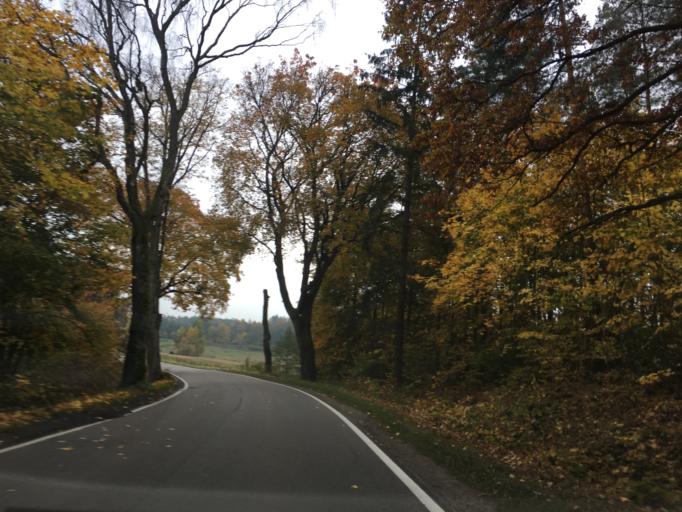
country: PL
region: Pomeranian Voivodeship
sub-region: Powiat wejherowski
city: Luzino
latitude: 54.4694
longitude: 18.0934
